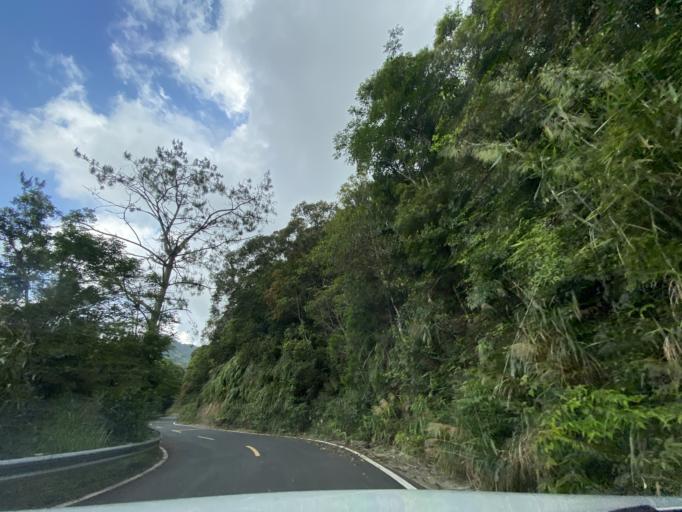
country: CN
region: Hainan
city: Diaoluoshan
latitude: 18.7085
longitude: 109.8829
